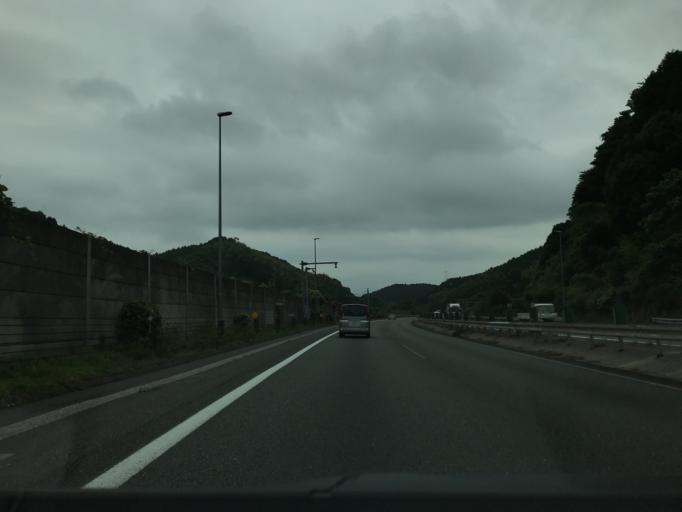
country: JP
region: Fukuoka
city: Nishifukuma
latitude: 33.7517
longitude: 130.5675
